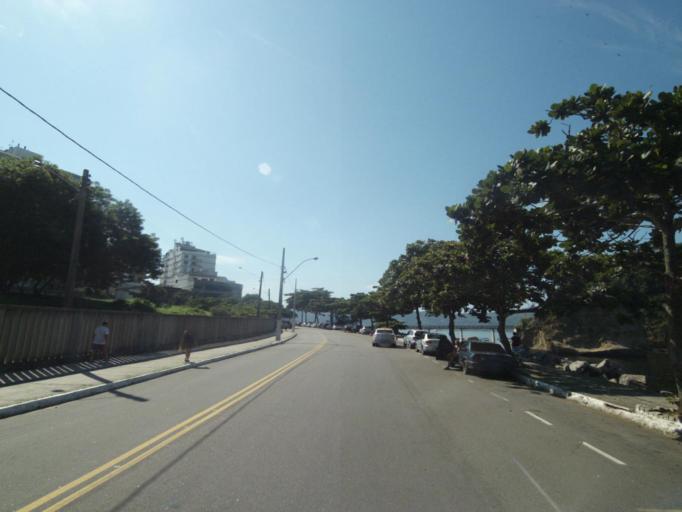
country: BR
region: Rio de Janeiro
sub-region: Niteroi
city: Niteroi
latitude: -22.9079
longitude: -43.1319
